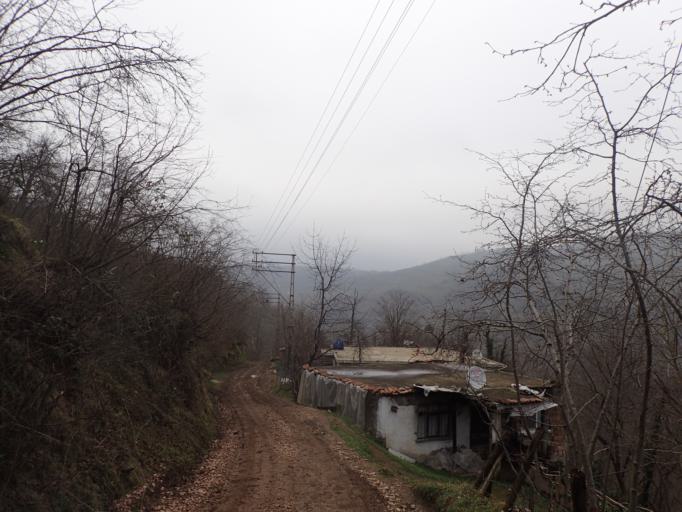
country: TR
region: Ordu
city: Camas
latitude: 40.9217
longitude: 37.5642
